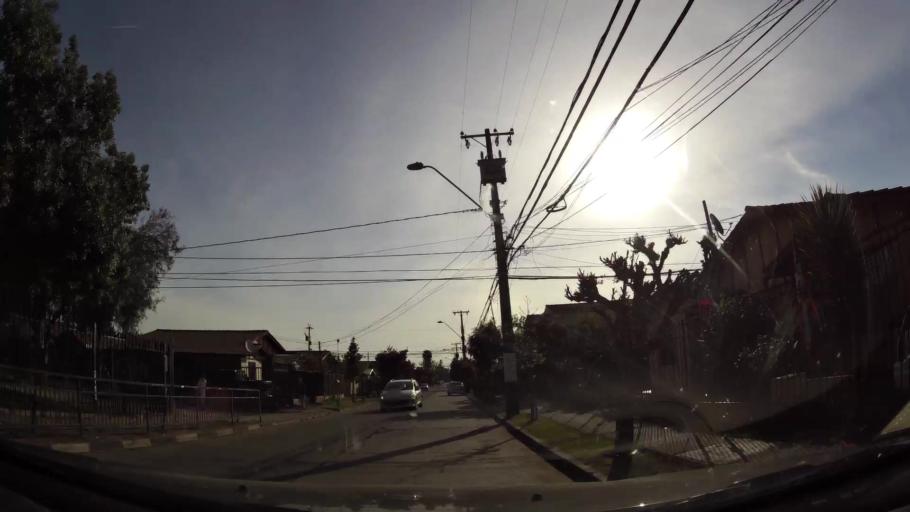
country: CL
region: Santiago Metropolitan
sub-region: Provincia de Cordillera
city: Puente Alto
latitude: -33.5781
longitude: -70.5658
